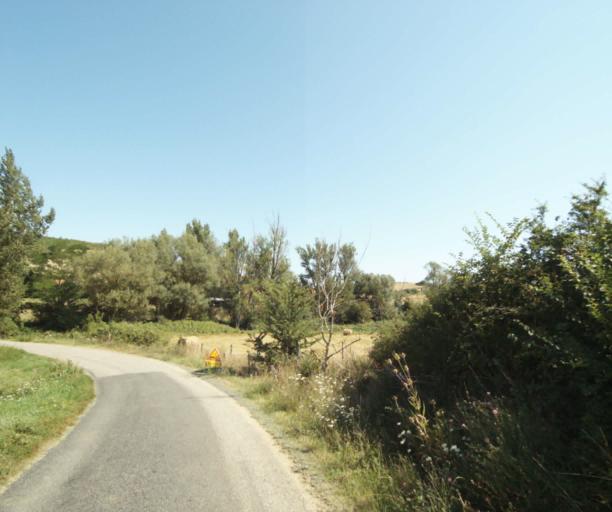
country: FR
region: Midi-Pyrenees
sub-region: Departement de l'Ariege
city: Lezat-sur-Leze
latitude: 43.2516
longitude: 1.3731
